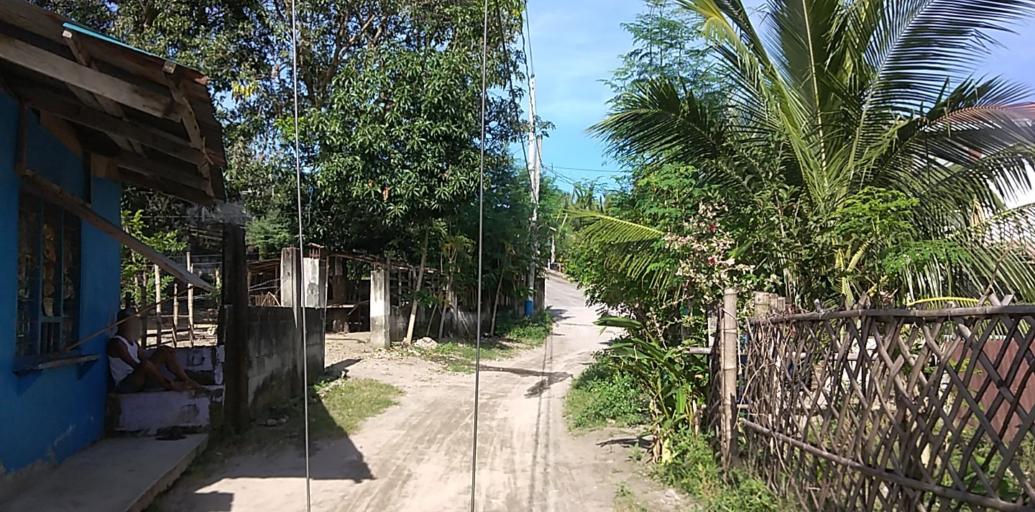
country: PH
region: Central Luzon
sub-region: Province of Pampanga
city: Porac
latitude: 15.0777
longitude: 120.5392
